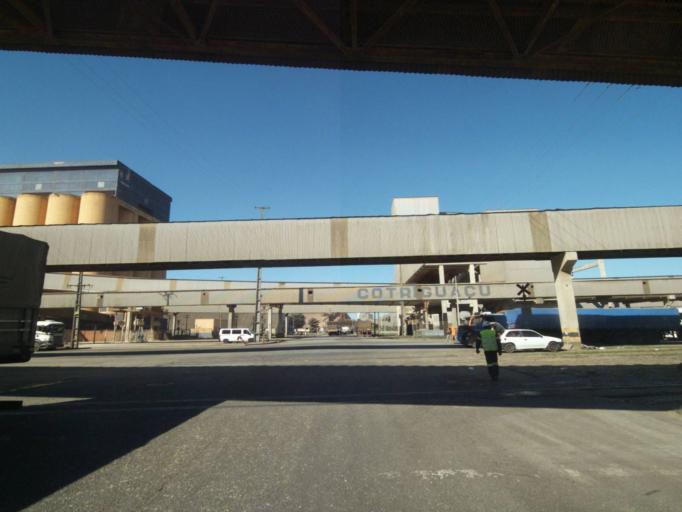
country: BR
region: Parana
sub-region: Paranagua
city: Paranagua
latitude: -25.5044
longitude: -48.5095
